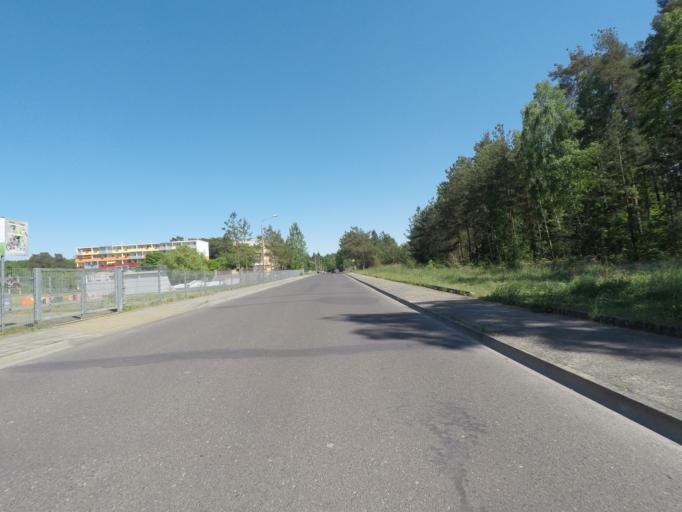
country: DE
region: Brandenburg
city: Eberswalde
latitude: 52.8281
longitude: 13.7629
